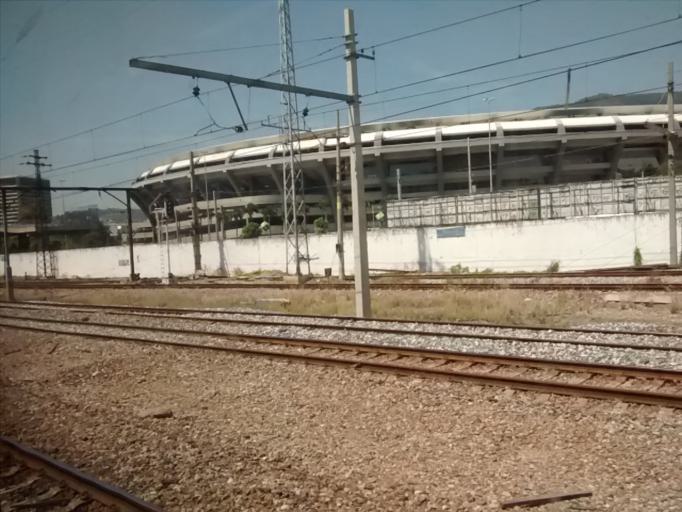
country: BR
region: Rio de Janeiro
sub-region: Rio De Janeiro
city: Rio de Janeiro
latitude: -22.9096
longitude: -43.2313
